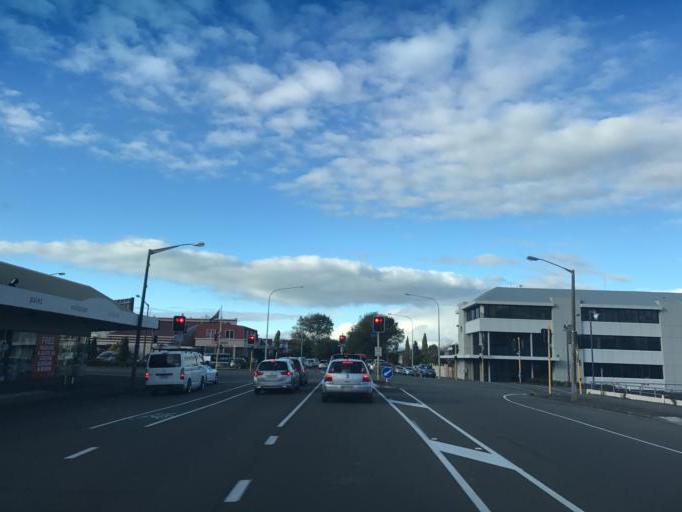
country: NZ
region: Manawatu-Wanganui
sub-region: Palmerston North City
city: Palmerston North
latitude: -40.3556
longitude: 175.6157
